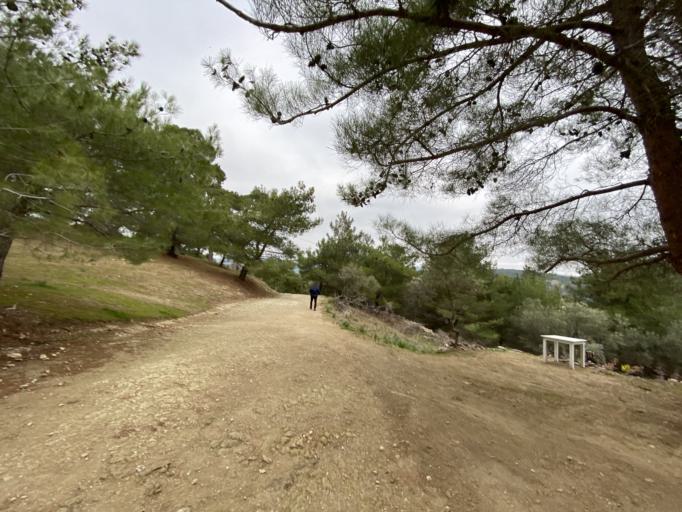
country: TR
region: Canakkale
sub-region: Merkez
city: Kucukkuyu
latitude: 39.5662
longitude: 26.6166
